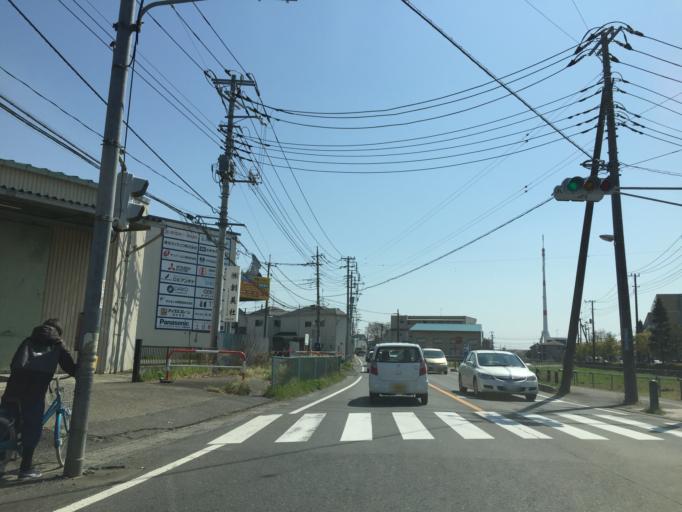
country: JP
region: Saitama
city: Yono
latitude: 35.8583
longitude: 139.6088
